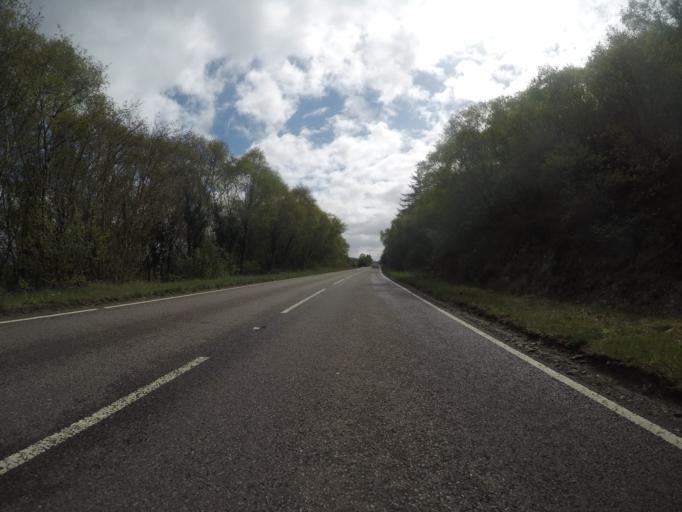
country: GB
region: Scotland
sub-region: Highland
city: Portree
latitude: 57.2617
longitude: -5.9466
